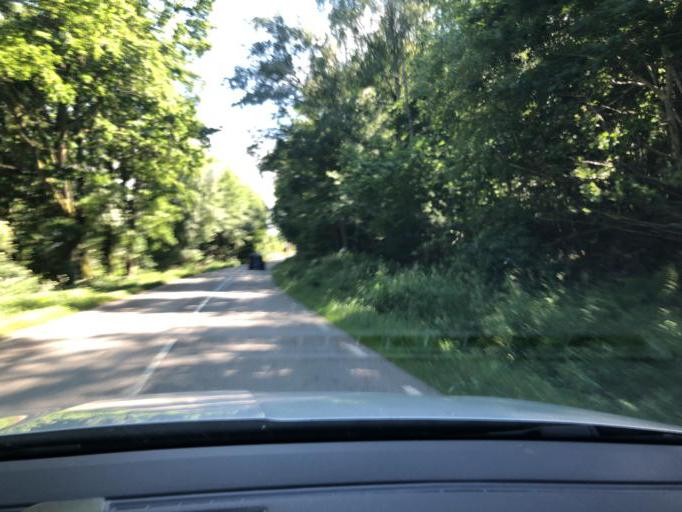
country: SE
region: Blekinge
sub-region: Solvesborgs Kommun
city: Soelvesborg
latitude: 56.1150
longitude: 14.6206
